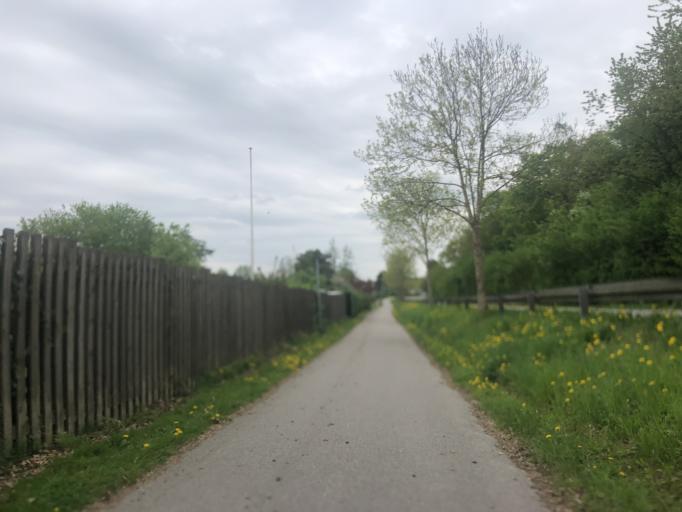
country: DK
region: Zealand
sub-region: Koge Kommune
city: Bjaeverskov
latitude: 55.4543
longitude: 12.0322
